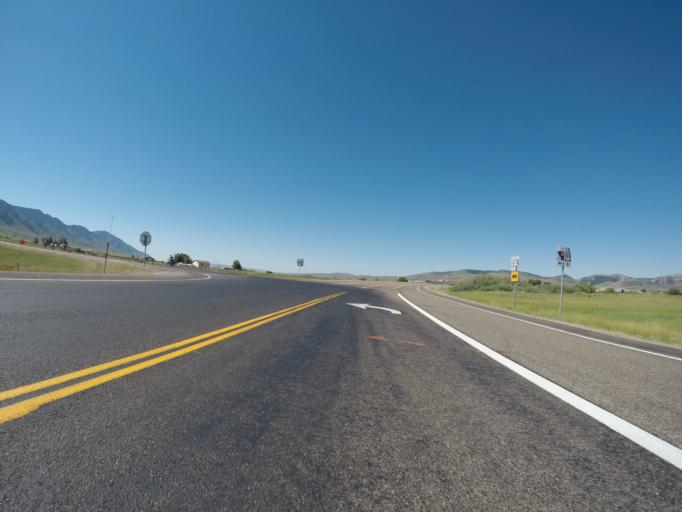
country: US
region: Idaho
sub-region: Bear Lake County
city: Montpelier
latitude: 42.3605
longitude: -111.0518
